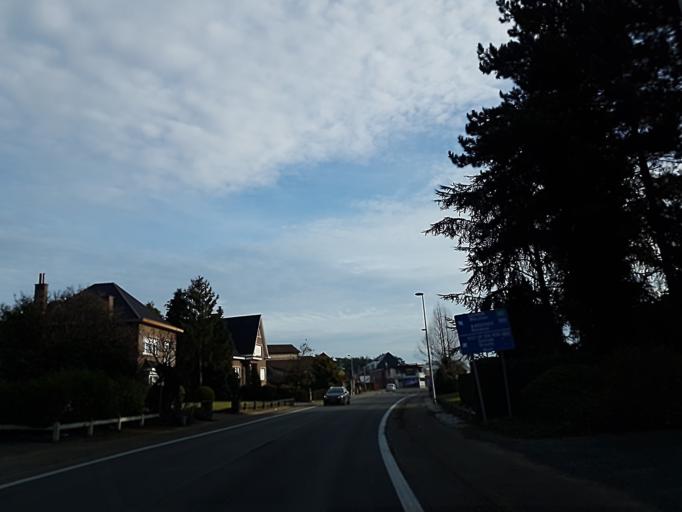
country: BE
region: Flanders
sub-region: Provincie Vlaams-Brabant
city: Tremelo
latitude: 50.9948
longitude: 4.6982
